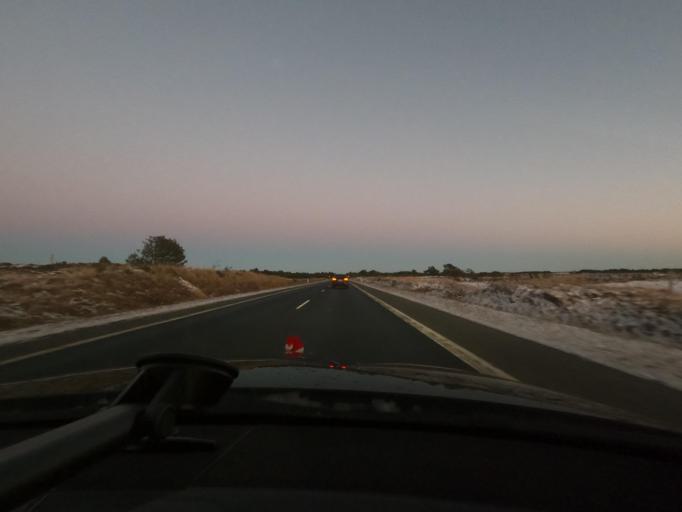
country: DE
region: Schleswig-Holstein
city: List
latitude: 55.1482
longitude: 8.5190
